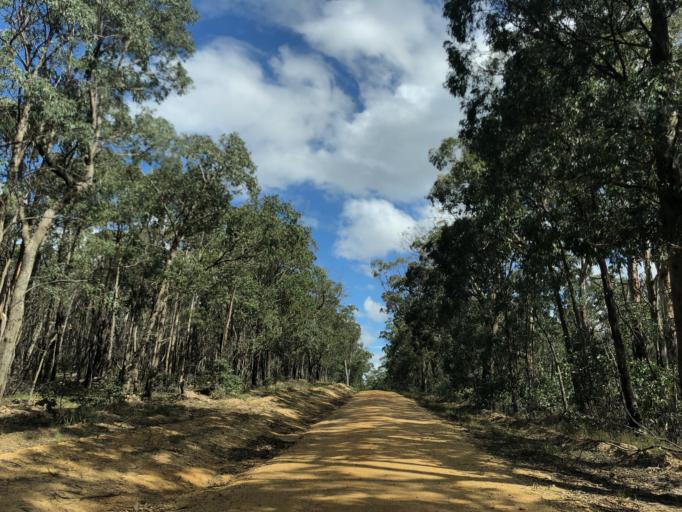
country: AU
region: Victoria
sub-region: Moorabool
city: Bacchus Marsh
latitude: -37.5219
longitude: 144.3225
